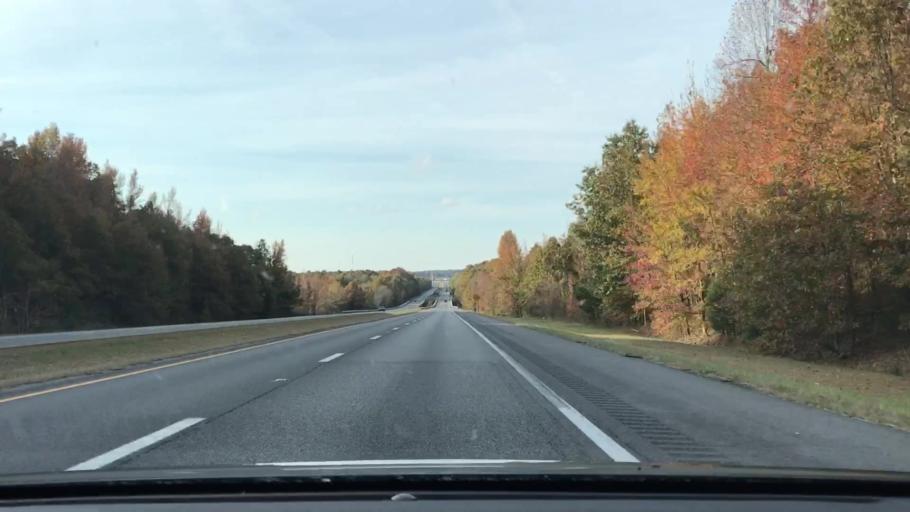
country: US
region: Kentucky
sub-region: Marshall County
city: Benton
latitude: 36.8907
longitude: -88.3517
